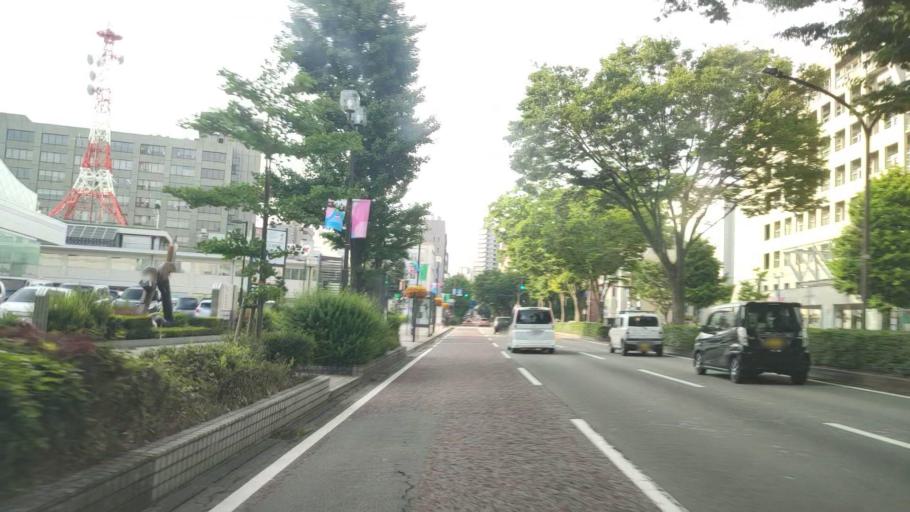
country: JP
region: Toyama
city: Toyama-shi
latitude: 36.6953
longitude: 137.2129
